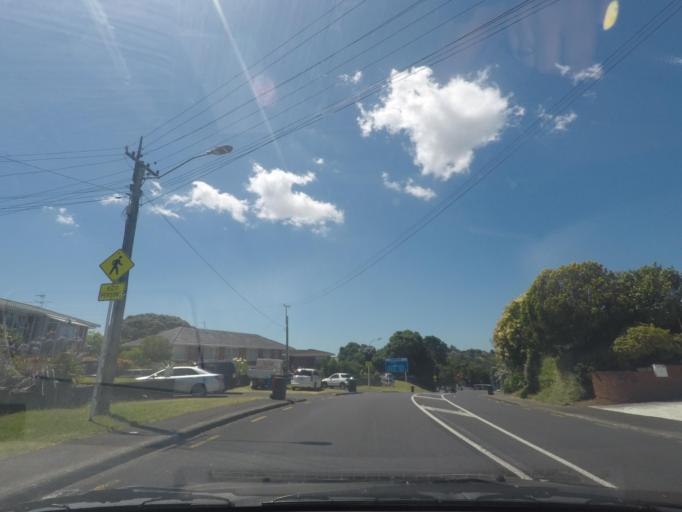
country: NZ
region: Auckland
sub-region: Auckland
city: Auckland
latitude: -36.9105
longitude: 174.7579
